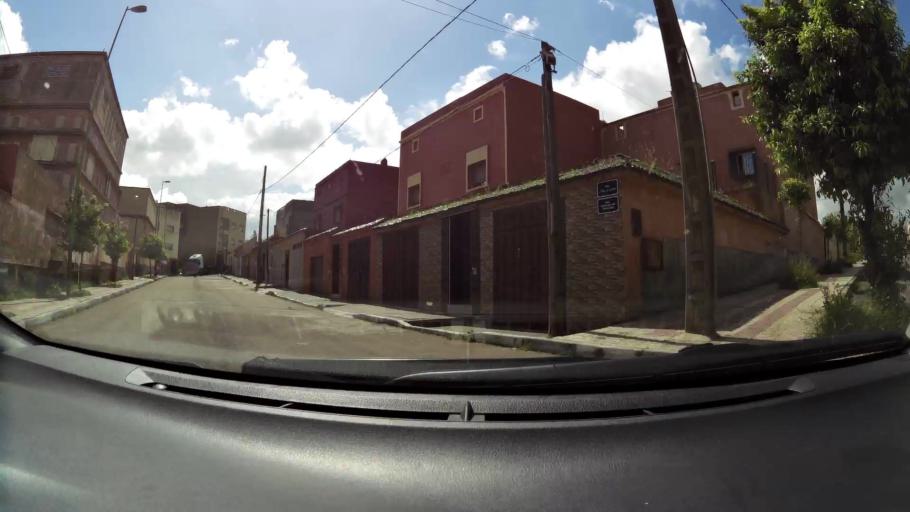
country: MA
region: Grand Casablanca
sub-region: Mediouna
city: Tit Mellil
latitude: 33.5518
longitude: -7.4874
